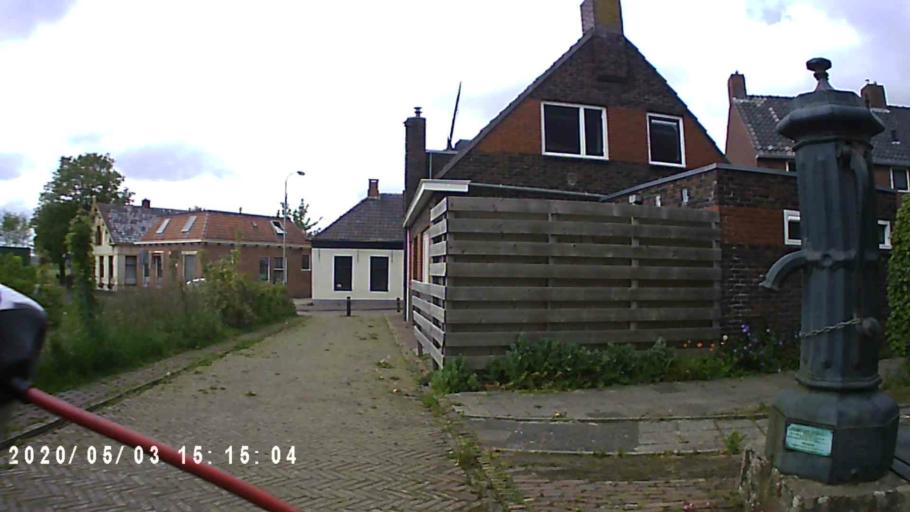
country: NL
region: Groningen
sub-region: Gemeente Winsum
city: Winsum
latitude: 53.3653
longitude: 6.4595
